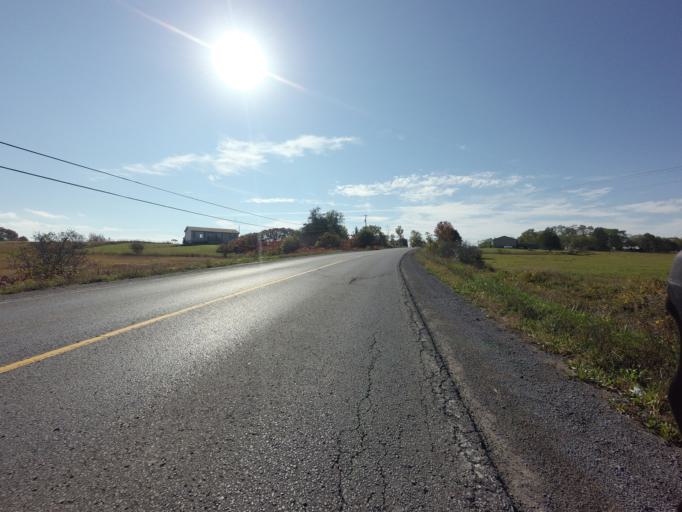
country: CA
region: Ontario
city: Prince Edward
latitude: 44.0122
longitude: -77.3633
